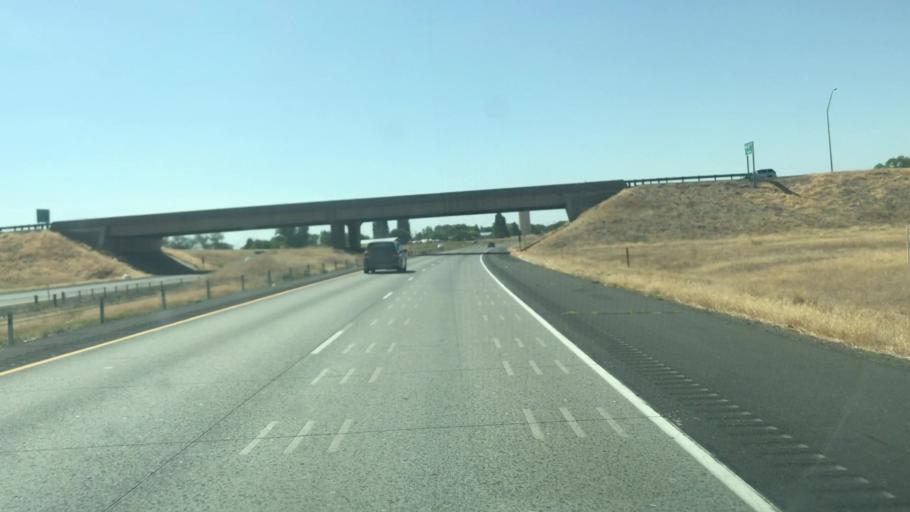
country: US
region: Washington
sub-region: Benton County
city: Prosser
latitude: 46.2222
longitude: -119.7892
